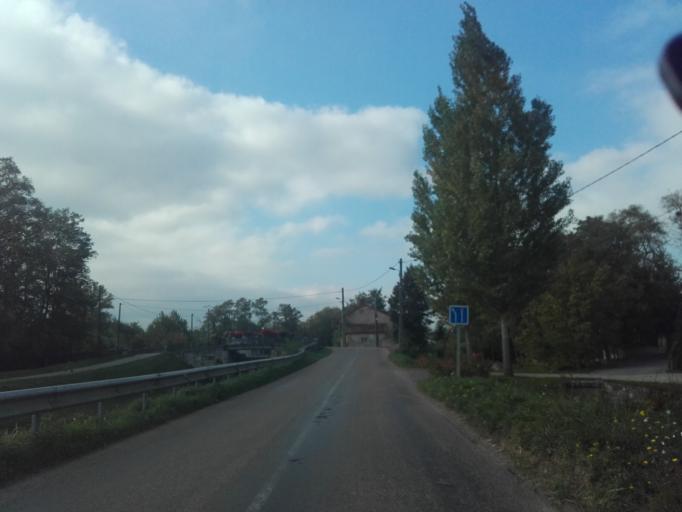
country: FR
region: Bourgogne
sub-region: Departement de Saone-et-Loire
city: Rully
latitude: 46.8815
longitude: 4.7672
